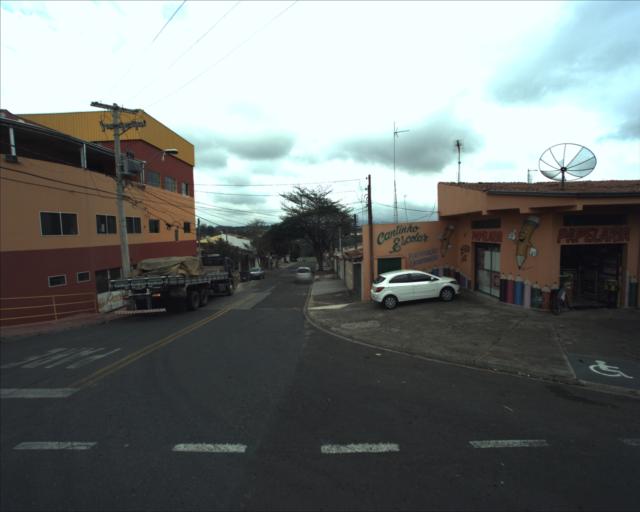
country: BR
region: Sao Paulo
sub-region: Sorocaba
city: Sorocaba
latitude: -23.4337
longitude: -47.5113
